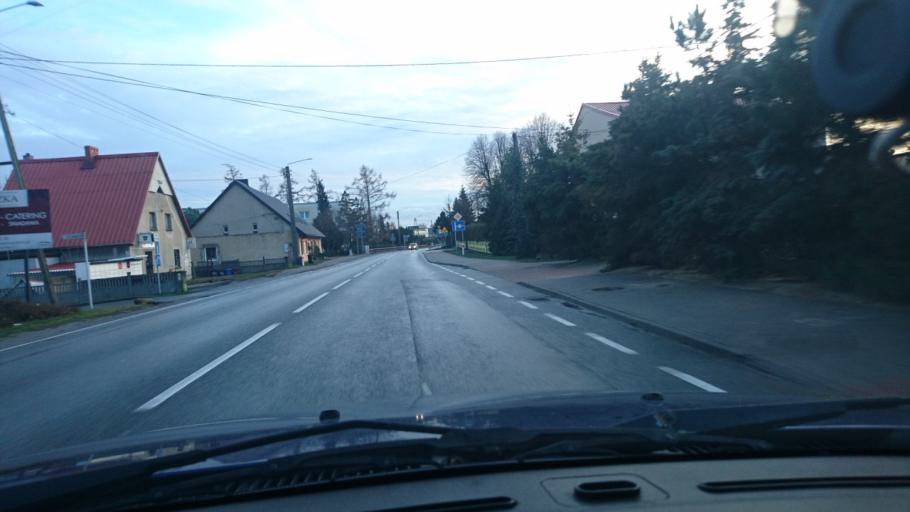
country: PL
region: Opole Voivodeship
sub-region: Powiat kluczborski
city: Byczyna
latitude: 51.1161
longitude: 18.2092
